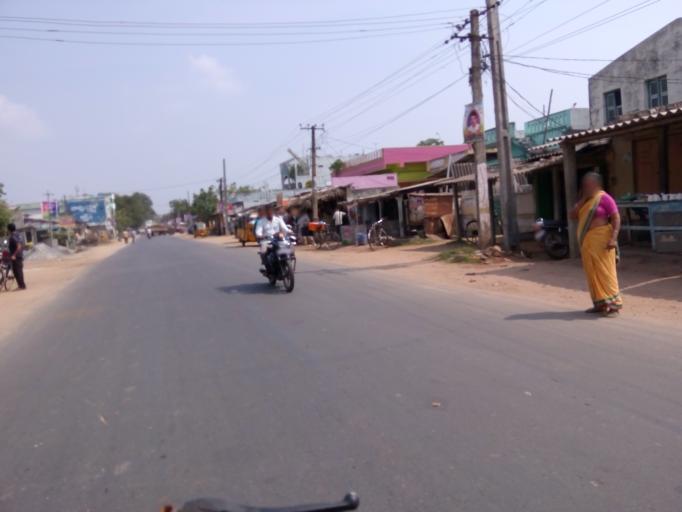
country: IN
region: Andhra Pradesh
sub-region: Prakasam
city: Chirala
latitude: 15.8477
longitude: 80.3840
